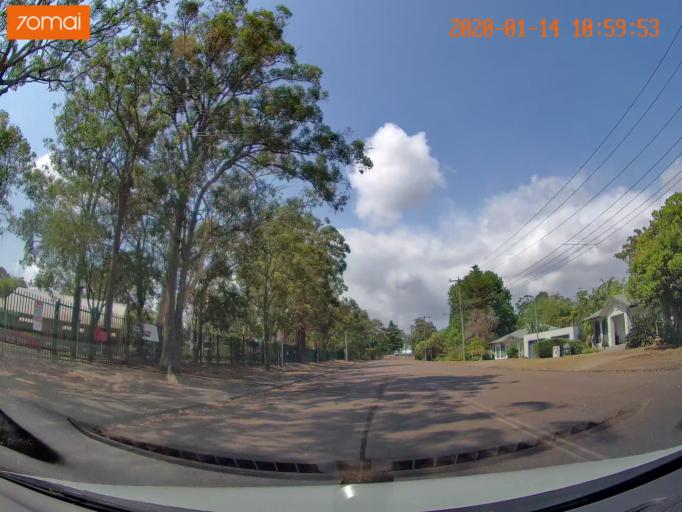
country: AU
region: New South Wales
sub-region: Lake Macquarie Shire
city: Dora Creek
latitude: -33.1030
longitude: 151.4884
